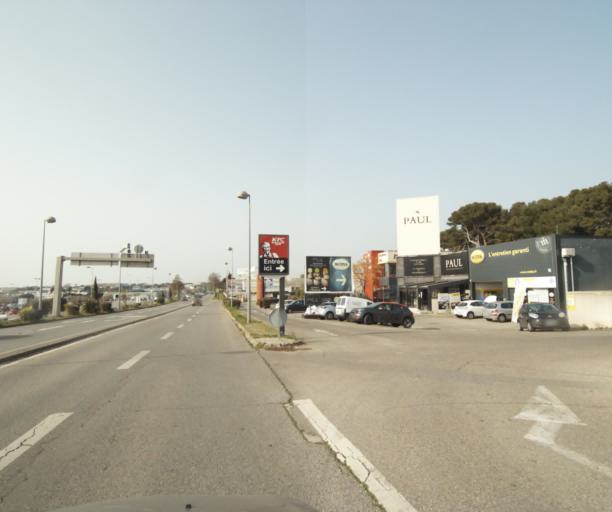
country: FR
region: Provence-Alpes-Cote d'Azur
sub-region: Departement des Bouches-du-Rhone
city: Vitrolles
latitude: 43.4326
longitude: 5.2637
